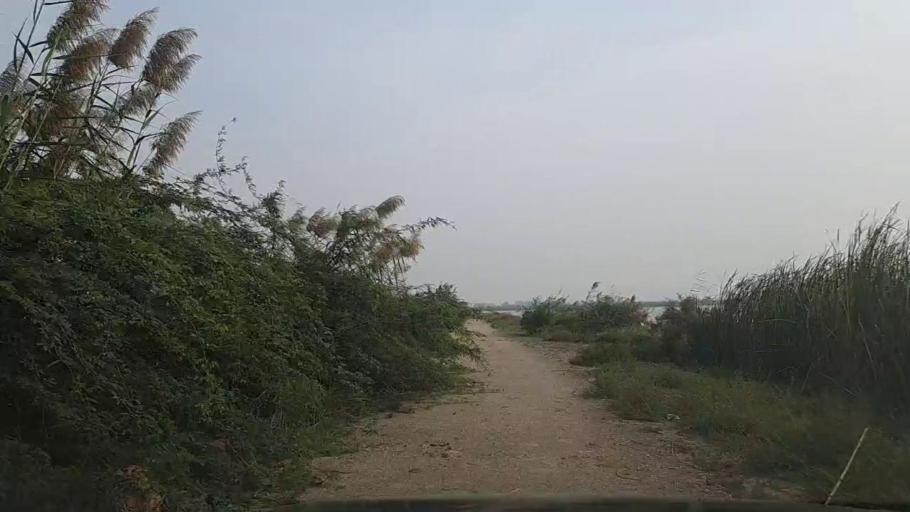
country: PK
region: Sindh
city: Chuhar Jamali
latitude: 24.5058
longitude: 67.8953
